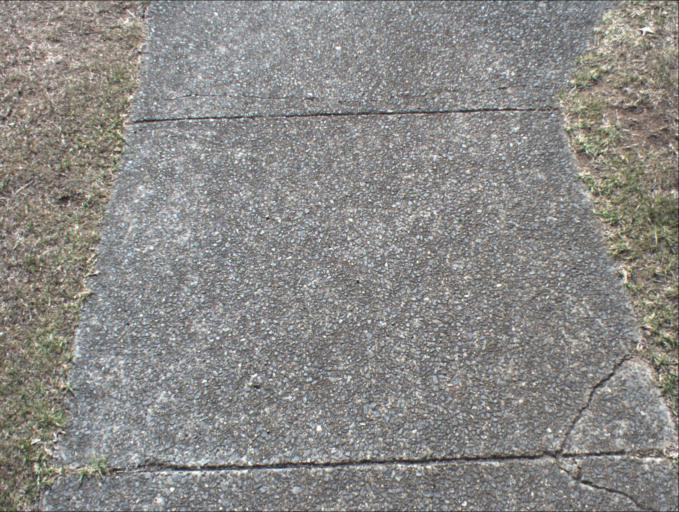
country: AU
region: Queensland
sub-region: Logan
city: Beenleigh
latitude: -27.6919
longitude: 153.2122
